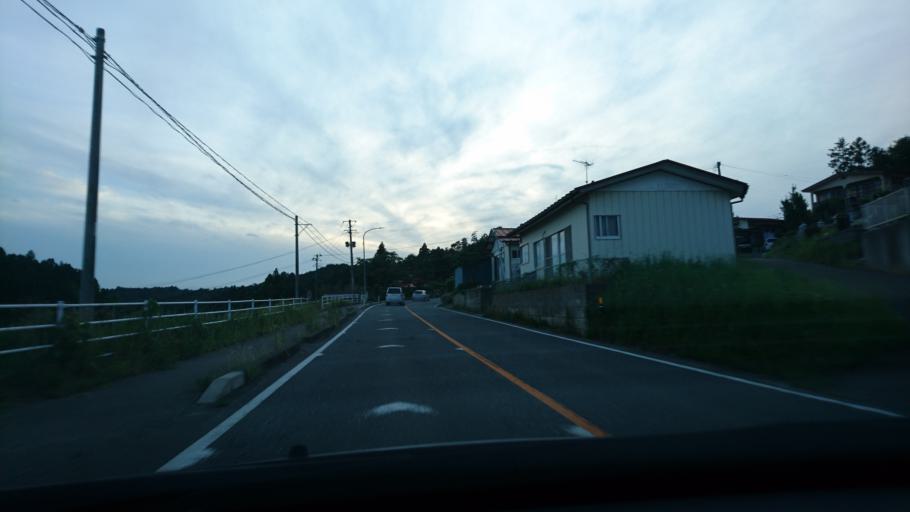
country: JP
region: Miyagi
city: Furukawa
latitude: 38.7543
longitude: 141.0084
